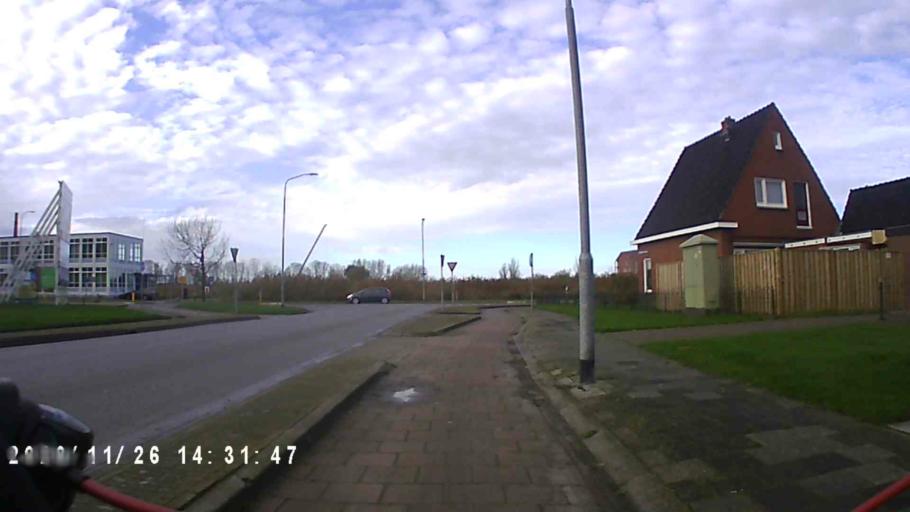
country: NL
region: Groningen
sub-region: Gemeente Appingedam
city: Appingedam
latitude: 53.3165
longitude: 6.8598
